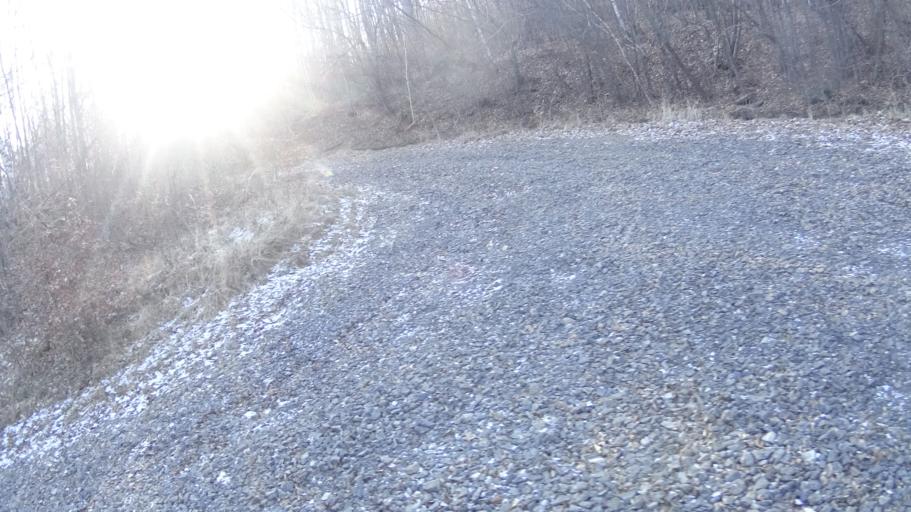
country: HU
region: Heves
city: Paradsasvar
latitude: 47.8889
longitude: 19.9437
